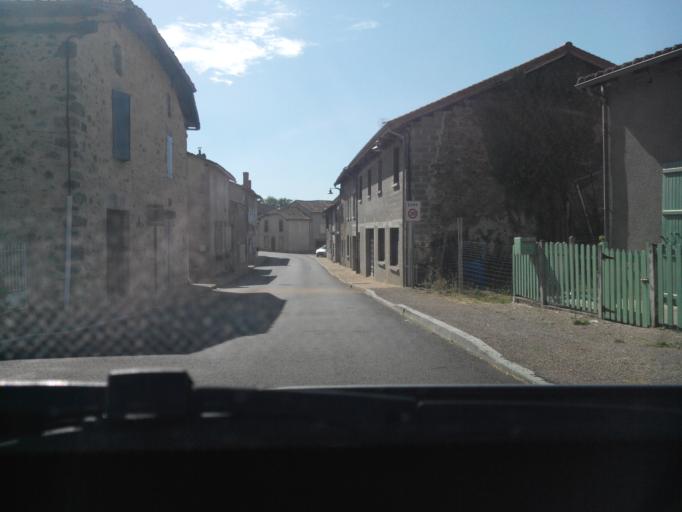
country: FR
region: Poitou-Charentes
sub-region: Departement de la Charente
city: Etagnac
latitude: 45.9512
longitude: 0.7830
